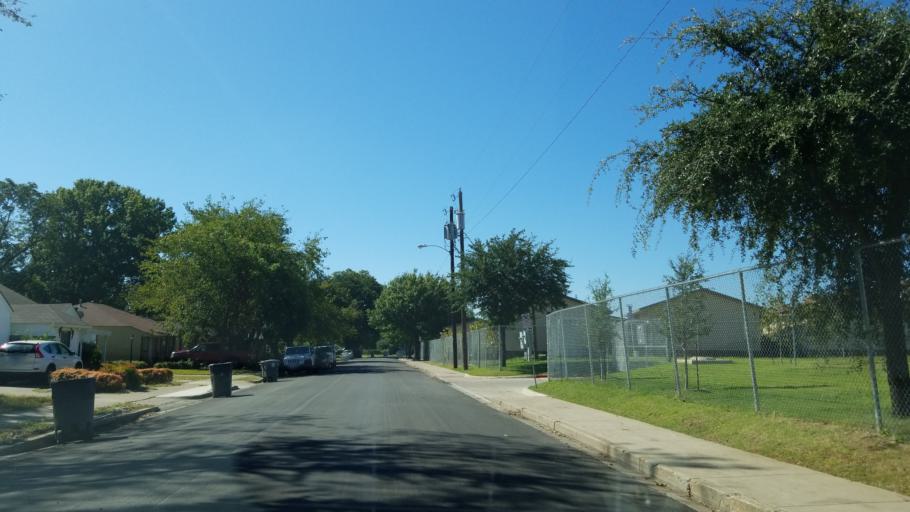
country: US
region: Texas
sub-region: Dallas County
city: Highland Park
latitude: 32.8061
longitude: -96.7482
